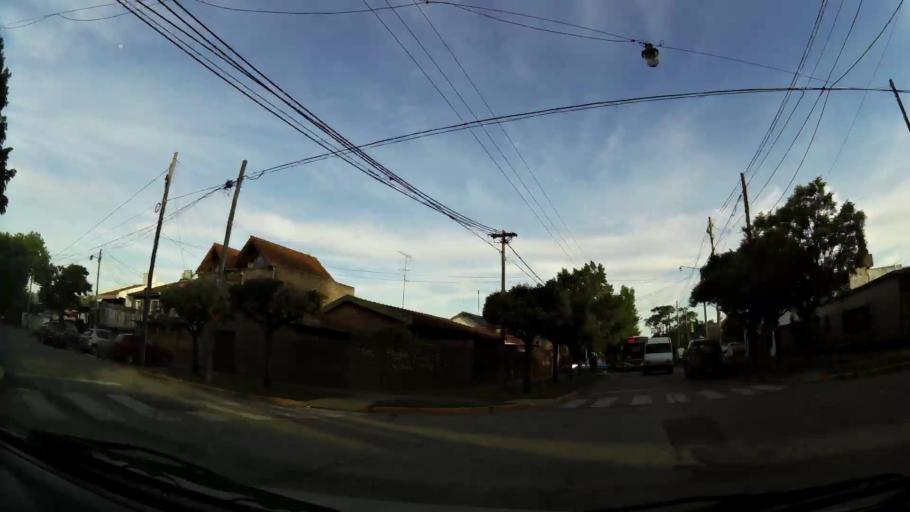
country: AR
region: Buenos Aires
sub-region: Partido de Almirante Brown
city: Adrogue
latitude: -34.7932
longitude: -58.3532
